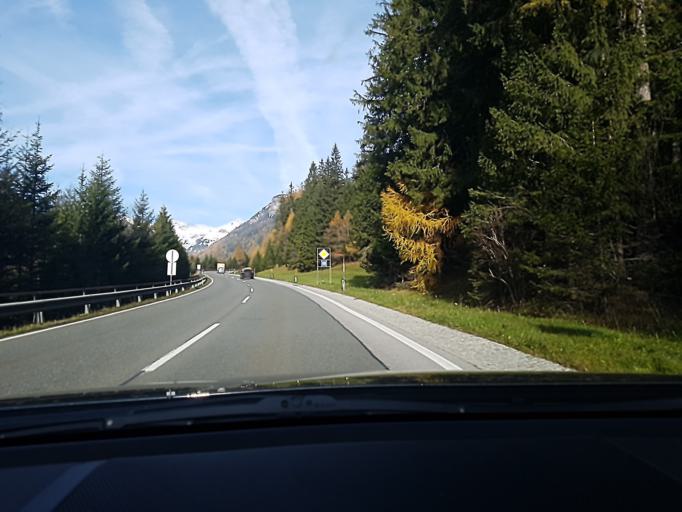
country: AT
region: Salzburg
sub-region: Politischer Bezirk Tamsweg
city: Tweng
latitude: 47.1938
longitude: 13.5960
